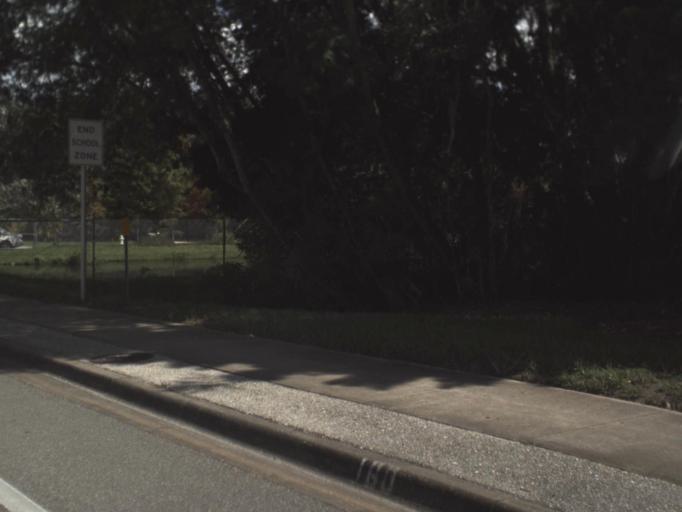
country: US
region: Florida
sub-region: Sarasota County
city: Kensington Park
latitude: 27.3374
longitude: -82.4851
